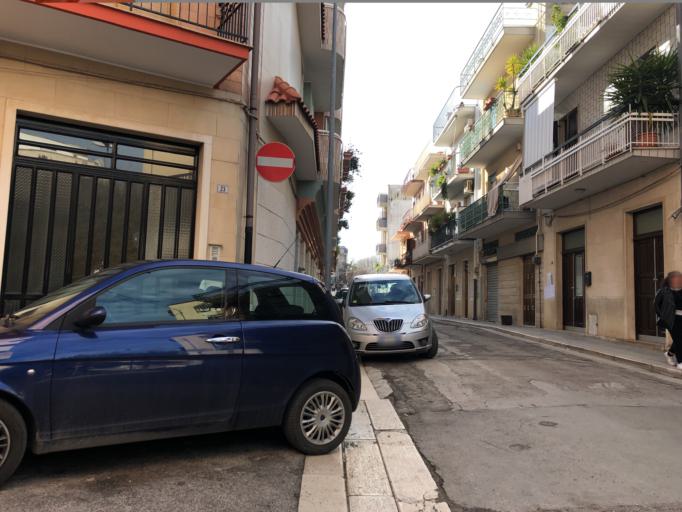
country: IT
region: Apulia
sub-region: Provincia di Barletta - Andria - Trani
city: Andria
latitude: 41.2265
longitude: 16.3080
